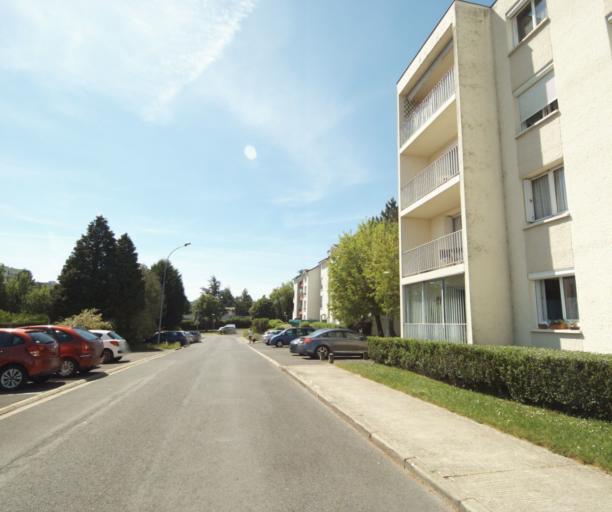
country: FR
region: Champagne-Ardenne
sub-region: Departement des Ardennes
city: La Francheville
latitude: 49.7466
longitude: 4.7185
